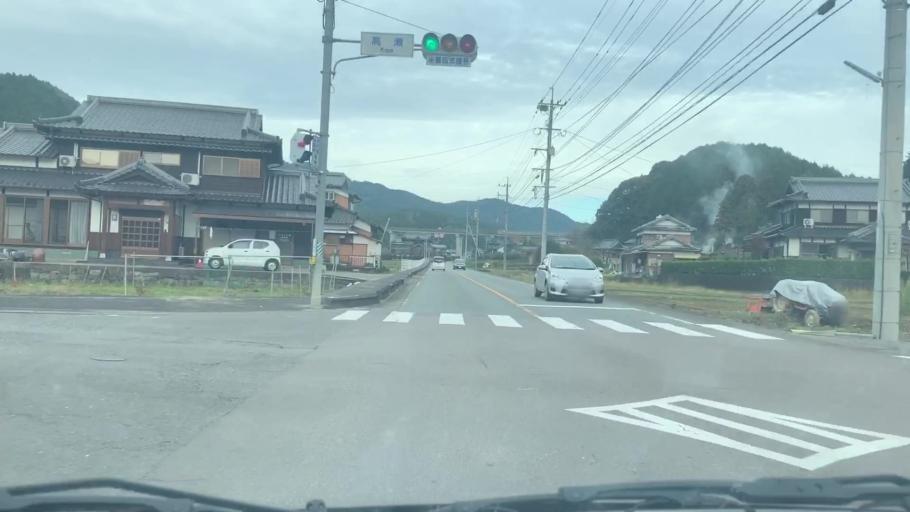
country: JP
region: Saga Prefecture
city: Ureshinomachi-shimojuku
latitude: 33.1400
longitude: 129.9783
